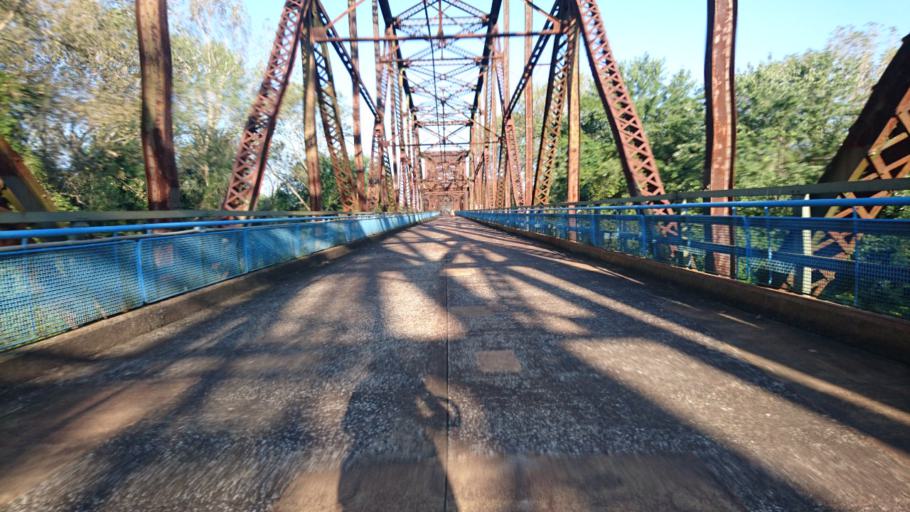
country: US
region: Missouri
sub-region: Saint Louis County
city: Glasgow Village
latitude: 38.7582
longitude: -90.1684
